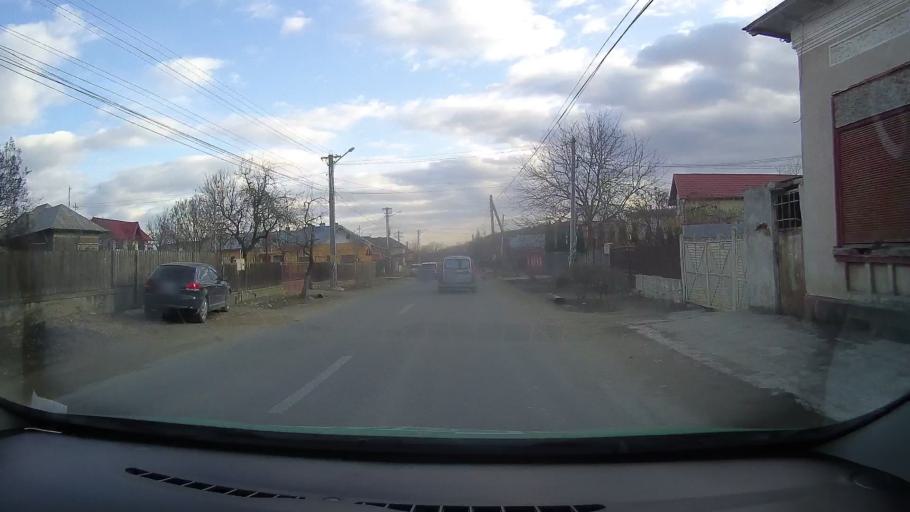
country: RO
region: Dambovita
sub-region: Comuna Gura Ocnitei
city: Gura Ocnitei
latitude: 44.9477
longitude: 25.5592
